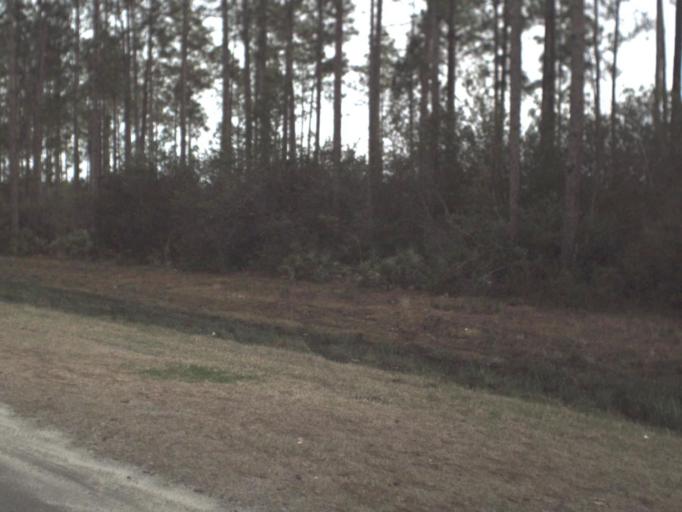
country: US
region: Florida
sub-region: Bay County
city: Callaway
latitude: 30.1385
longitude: -85.3897
